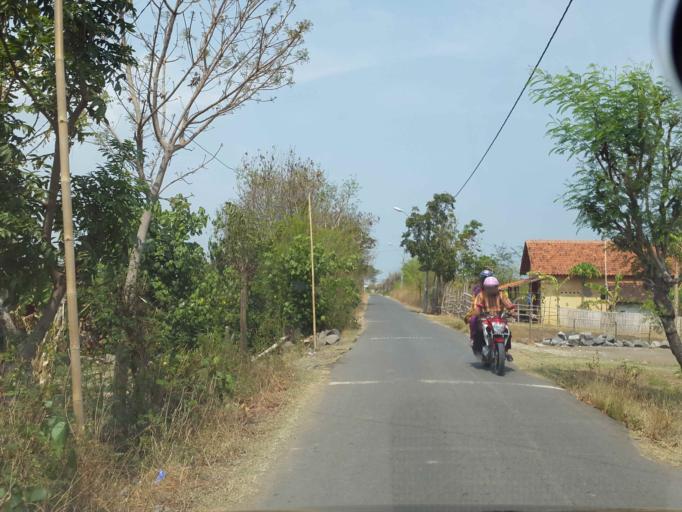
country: ID
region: Central Java
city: Dukuhturi
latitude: -6.8285
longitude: 109.0543
